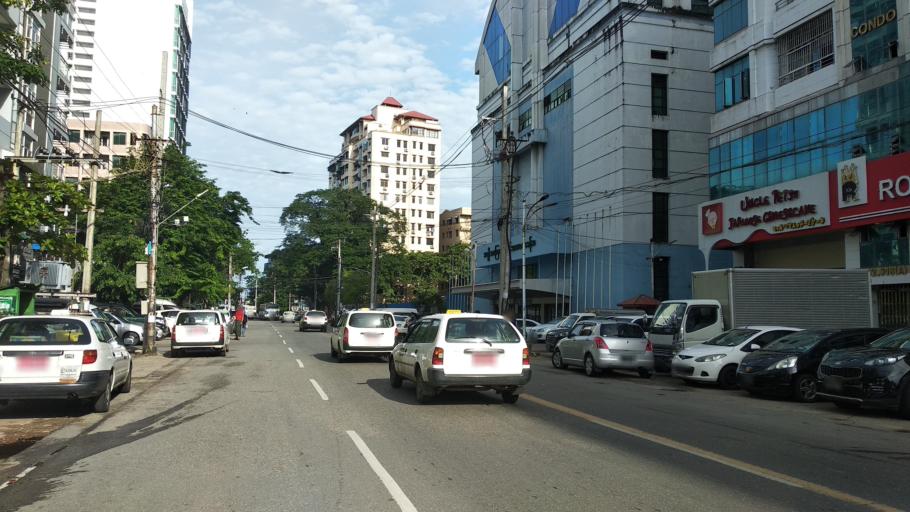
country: MM
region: Yangon
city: Yangon
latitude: 16.7776
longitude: 96.1389
